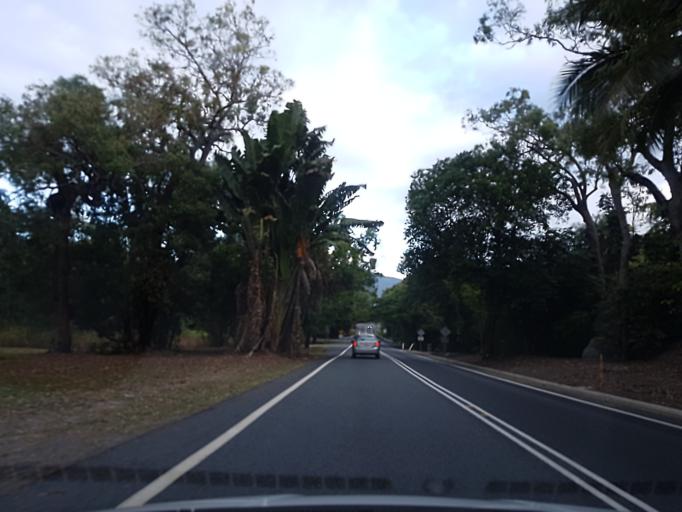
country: AU
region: Queensland
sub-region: Cairns
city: Palm Cove
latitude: -16.6540
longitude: 145.5640
